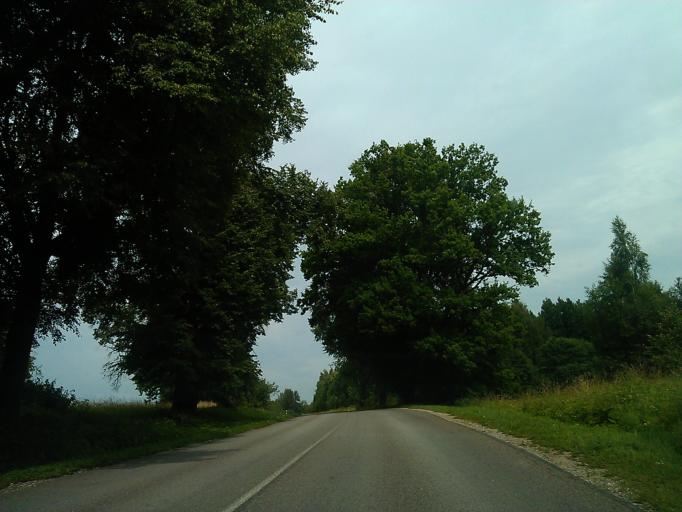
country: LV
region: Beverina
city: Murmuiza
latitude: 57.4269
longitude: 25.4391
